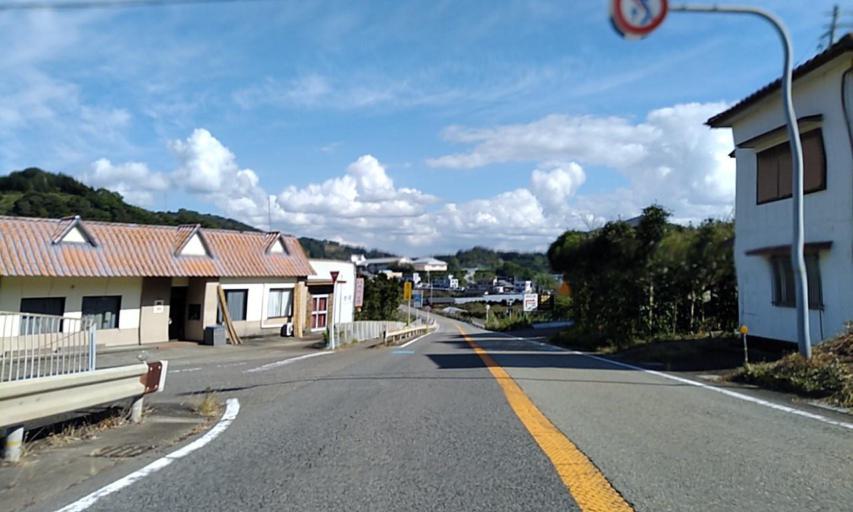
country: JP
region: Wakayama
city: Tanabe
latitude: 33.7819
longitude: 135.2751
